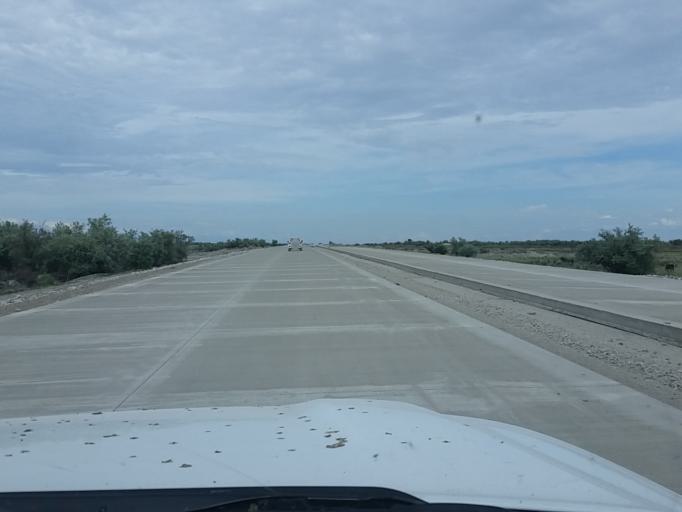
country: KZ
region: Almaty Oblysy
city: Zharkent
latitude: 44.0214
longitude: 79.8220
